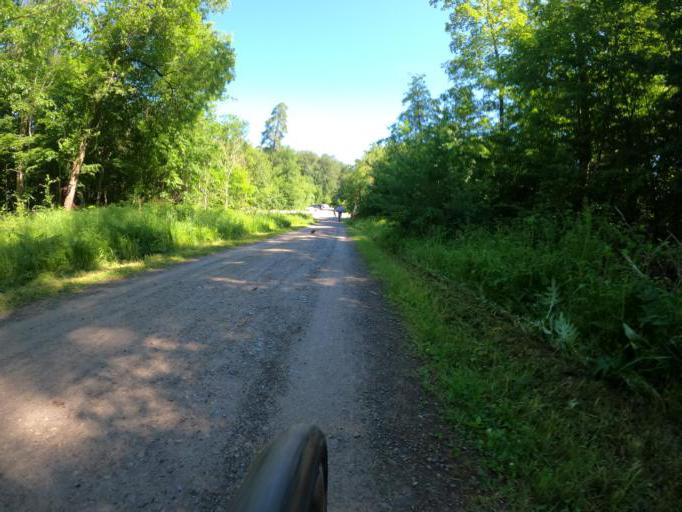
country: DE
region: Baden-Wuerttemberg
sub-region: Regierungsbezirk Stuttgart
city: Gerlingen
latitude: 48.7552
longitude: 9.1013
